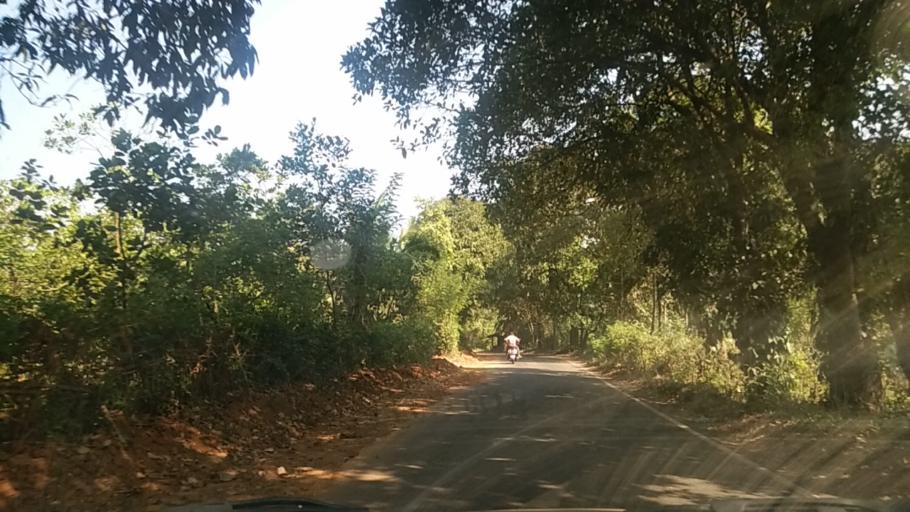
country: IN
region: Goa
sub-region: South Goa
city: Sanguem
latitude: 15.1886
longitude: 74.2270
